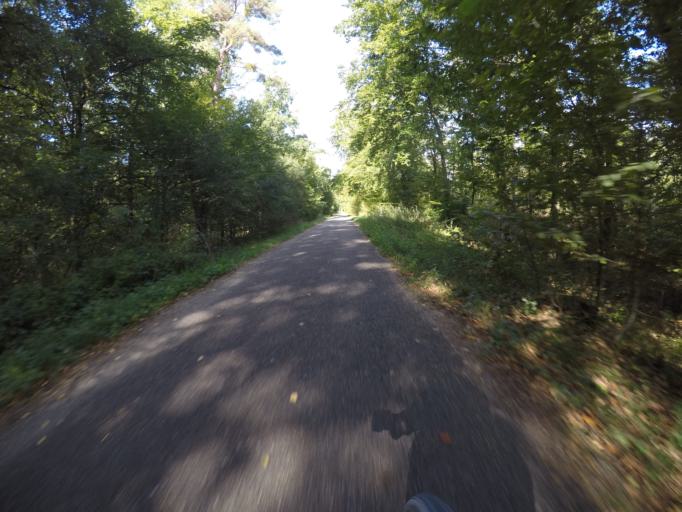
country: DE
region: Baden-Wuerttemberg
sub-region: Karlsruhe Region
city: Kronau
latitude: 49.2088
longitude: 8.6152
